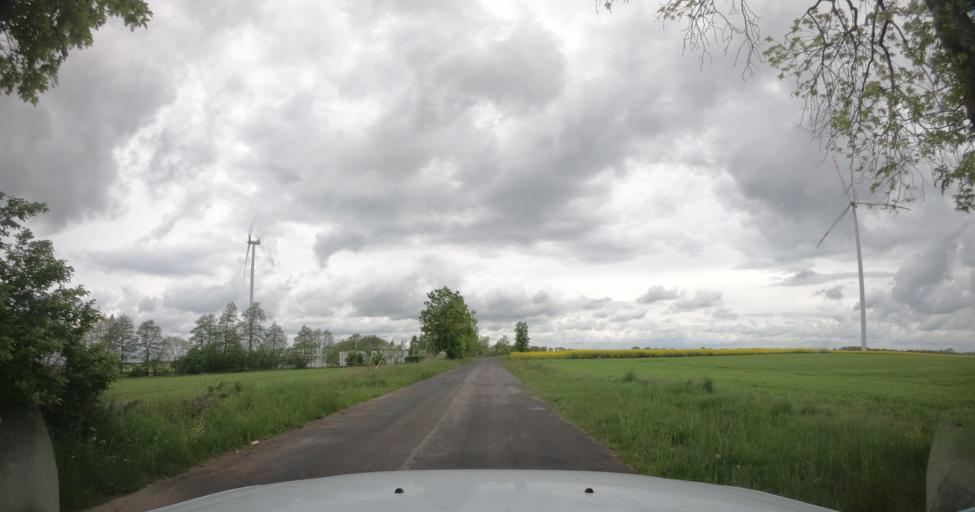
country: PL
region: West Pomeranian Voivodeship
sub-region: Powiat pyrzycki
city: Kozielice
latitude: 53.1142
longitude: 14.8128
